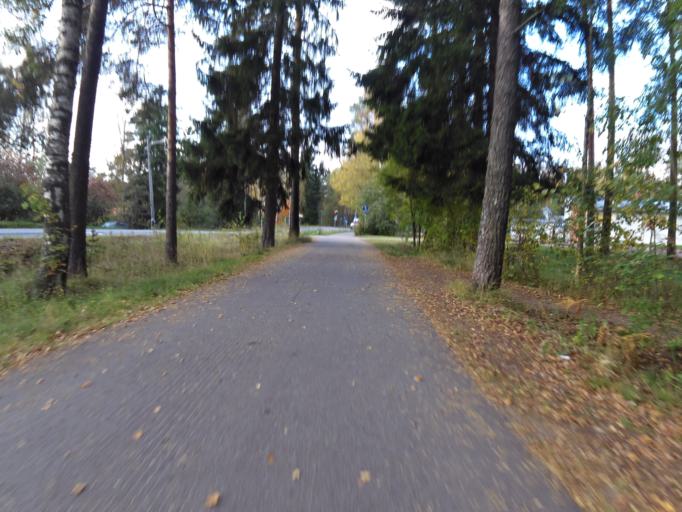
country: FI
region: Uusimaa
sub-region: Helsinki
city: Kauniainen
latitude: 60.2826
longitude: 24.7466
